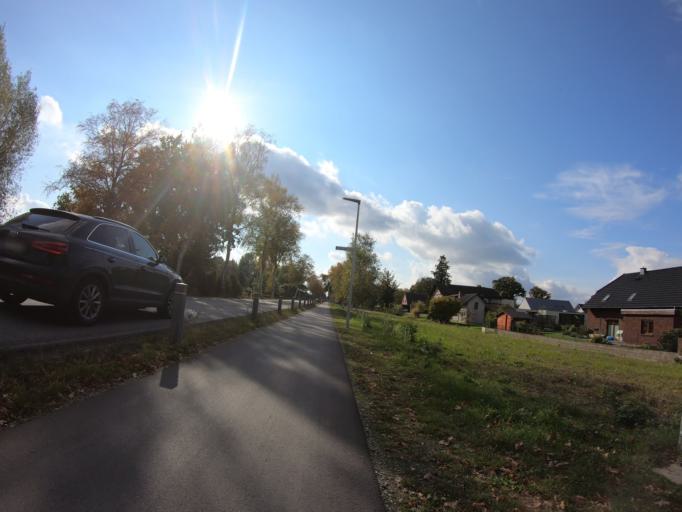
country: DE
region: Lower Saxony
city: Sassenburg
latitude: 52.5285
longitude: 10.5965
